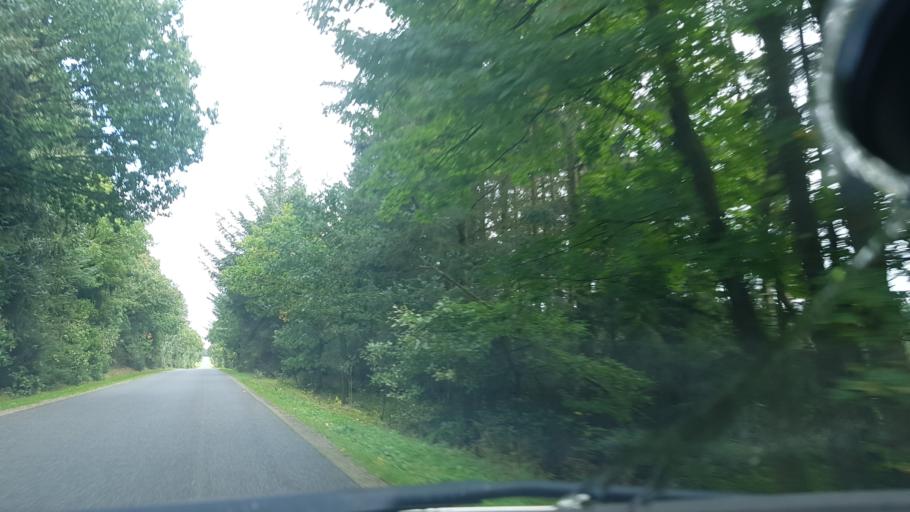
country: DK
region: South Denmark
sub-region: Vejen Kommune
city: Brorup
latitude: 55.6160
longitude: 9.0214
